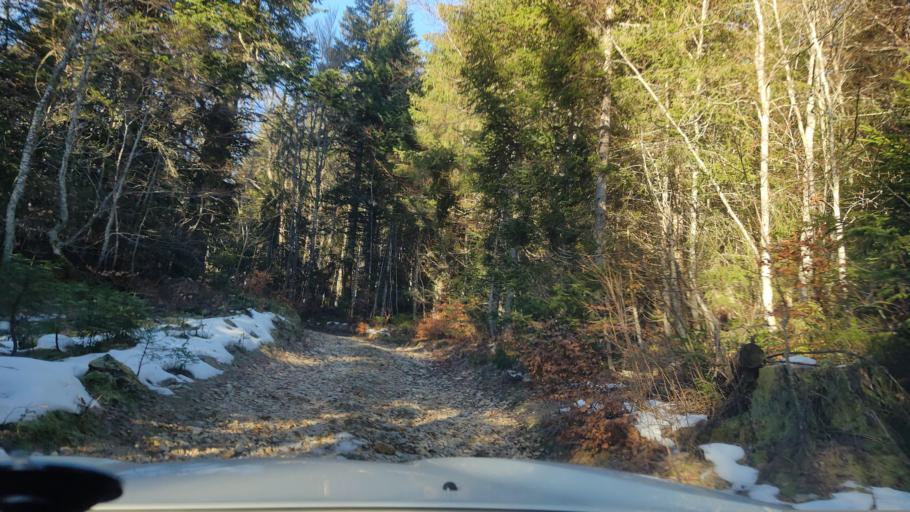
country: FR
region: Rhone-Alpes
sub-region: Departement de la Savoie
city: Mery
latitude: 45.6523
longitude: 5.9793
